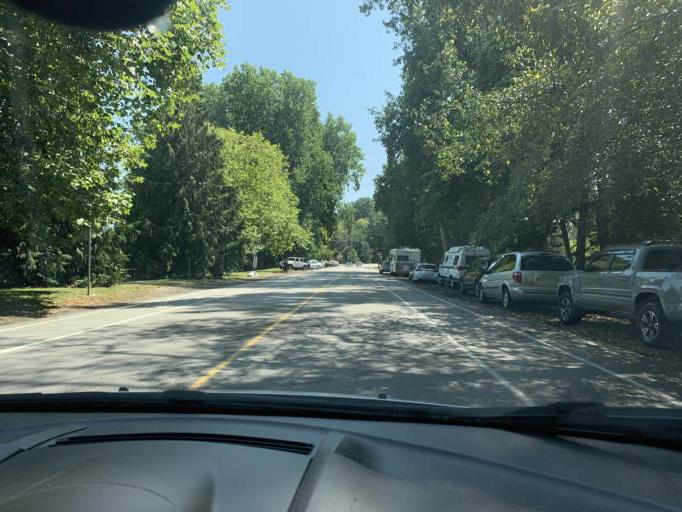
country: CA
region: British Columbia
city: West End
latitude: 49.2727
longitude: -123.2053
